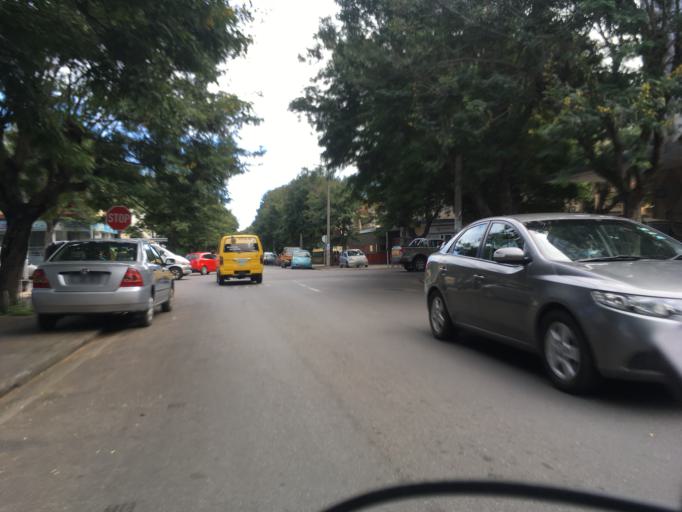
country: MZ
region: Maputo City
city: Maputo
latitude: -25.9672
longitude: 32.5927
